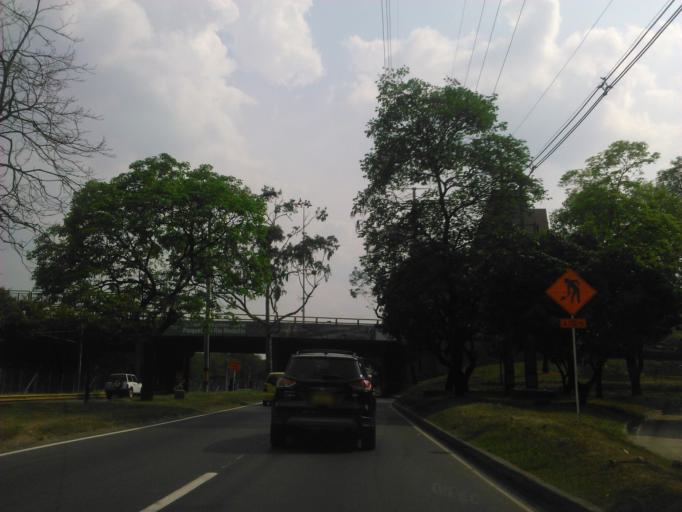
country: CO
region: Antioquia
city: Medellin
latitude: 6.2551
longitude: -75.5773
